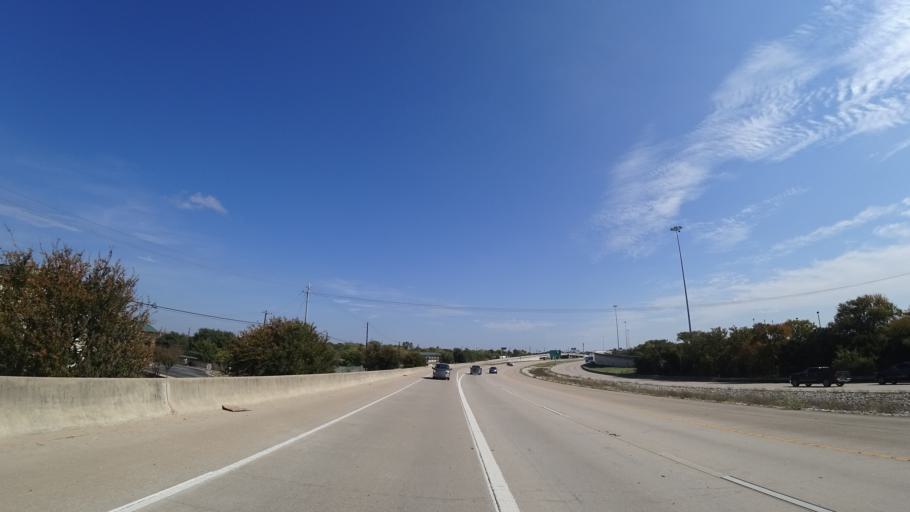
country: US
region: Texas
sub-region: Travis County
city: Rollingwood
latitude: 30.2338
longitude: -97.8131
